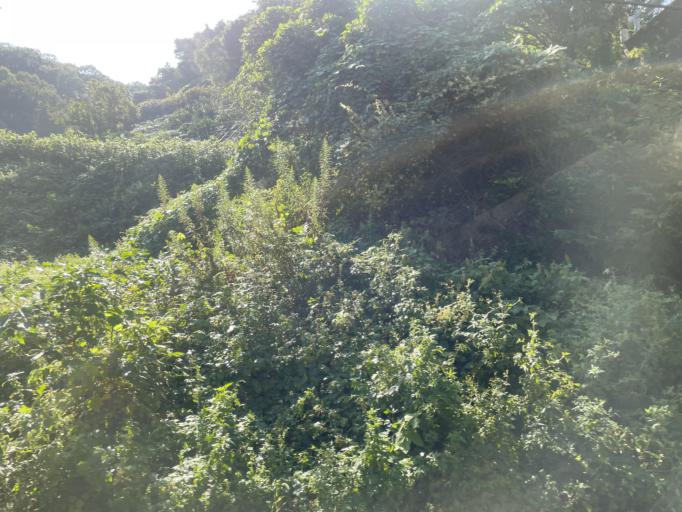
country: JP
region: Osaka
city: Kashihara
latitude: 34.5368
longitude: 135.6592
